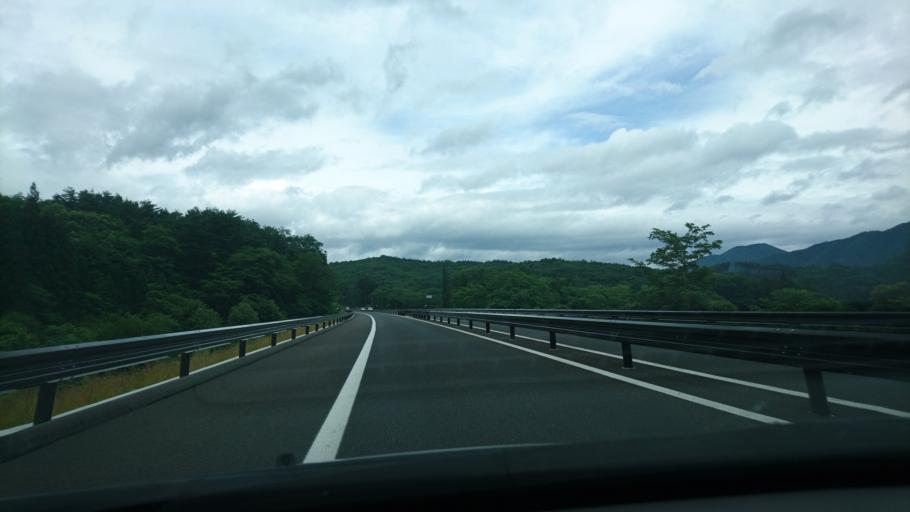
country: JP
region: Iwate
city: Yamada
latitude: 39.5440
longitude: 141.9232
